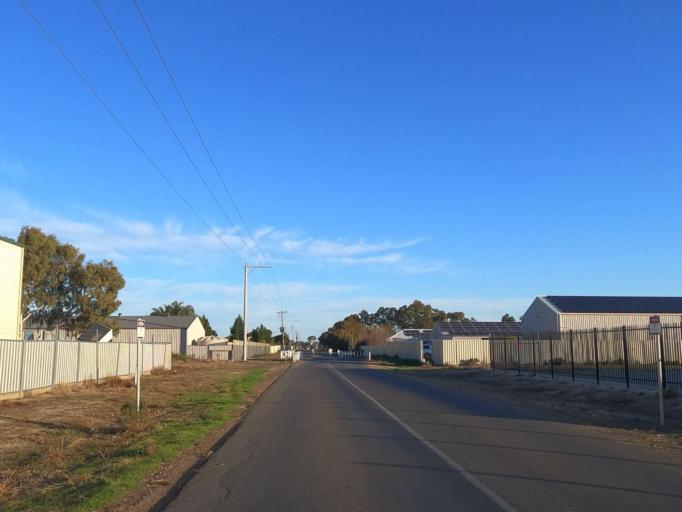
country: AU
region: Victoria
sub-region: Swan Hill
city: Swan Hill
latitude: -35.3285
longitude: 143.5349
